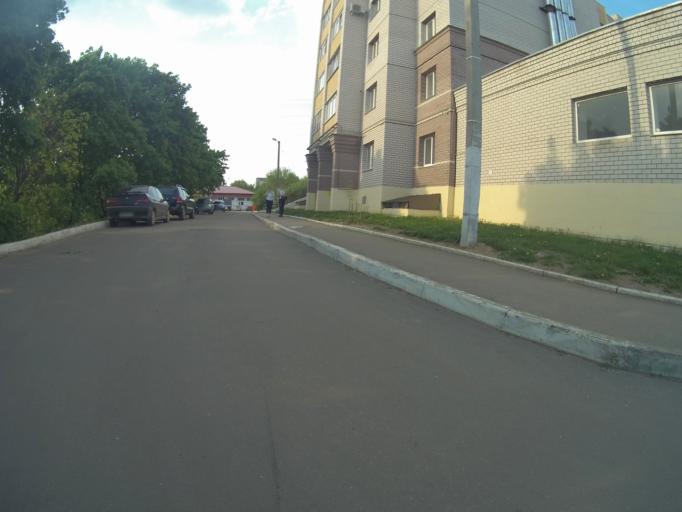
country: RU
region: Vladimir
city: Vladimir
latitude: 56.1690
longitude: 40.4408
